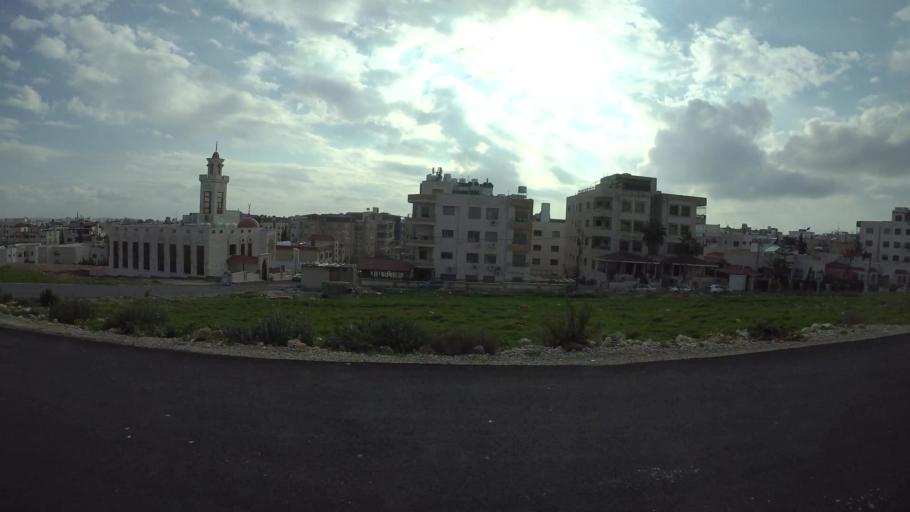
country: JO
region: Amman
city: Al Jubayhah
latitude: 31.9833
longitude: 35.8519
